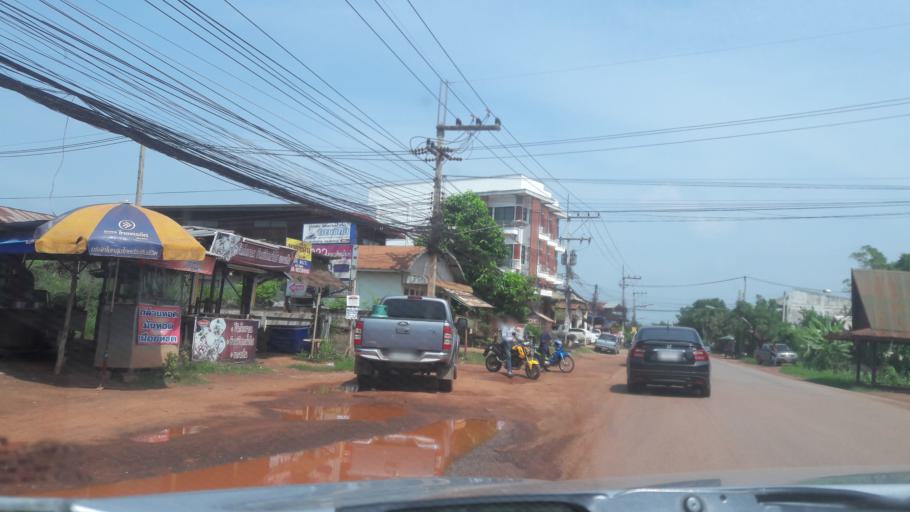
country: TH
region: Changwat Udon Thani
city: Udon Thani
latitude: 17.4314
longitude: 102.8238
